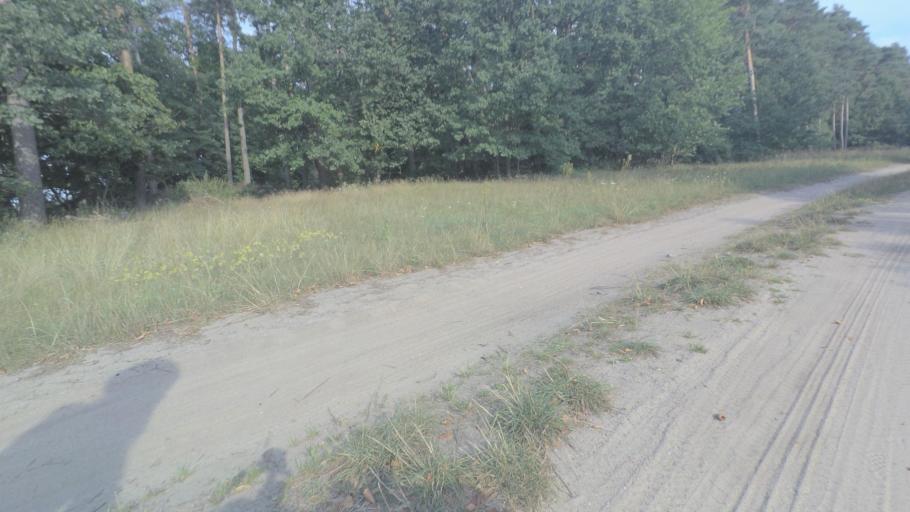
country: DE
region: Brandenburg
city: Wittstock
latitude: 53.2576
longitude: 12.4659
